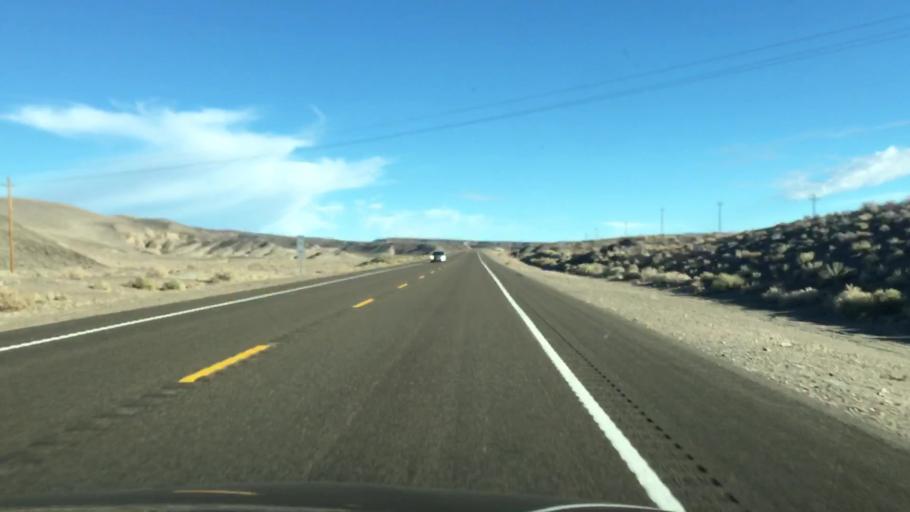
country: US
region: Nevada
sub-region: Mineral County
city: Hawthorne
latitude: 38.2379
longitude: -118.0329
